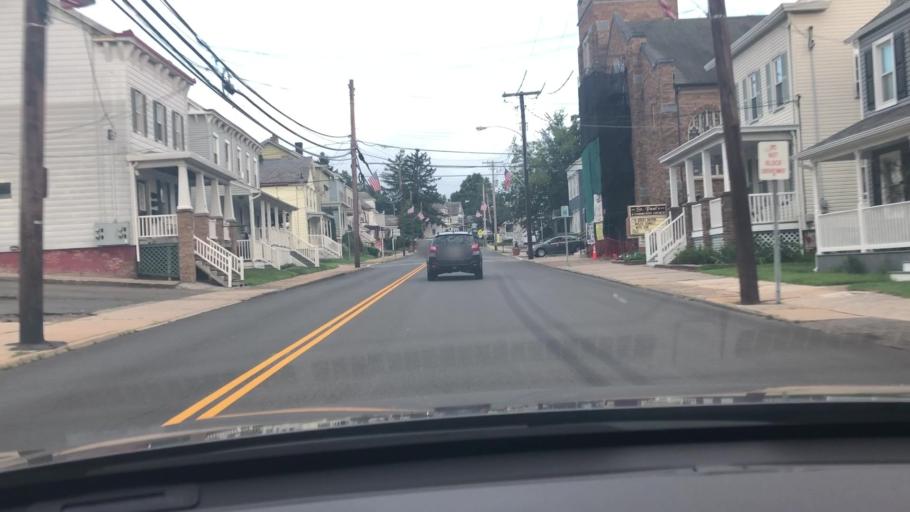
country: US
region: New Jersey
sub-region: Middlesex County
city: Milltown
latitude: 40.4497
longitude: -74.4350
